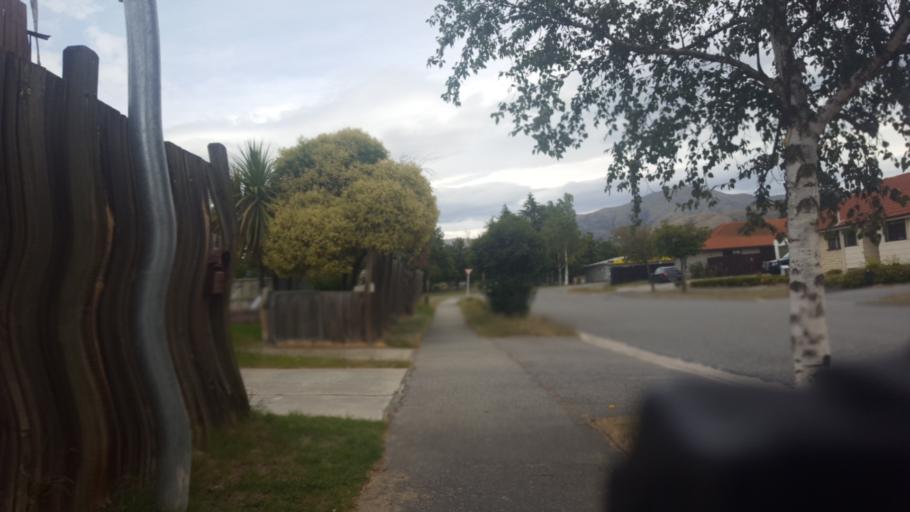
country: NZ
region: Otago
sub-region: Queenstown-Lakes District
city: Wanaka
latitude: -45.0420
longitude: 169.1903
